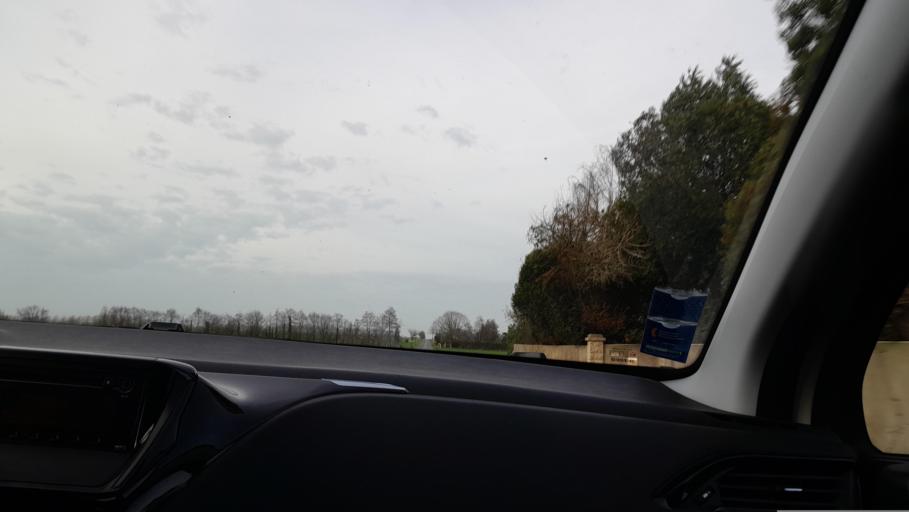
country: FR
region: Pays de la Loire
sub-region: Departement de la Mayenne
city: Ballots
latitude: 47.8950
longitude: -1.0564
